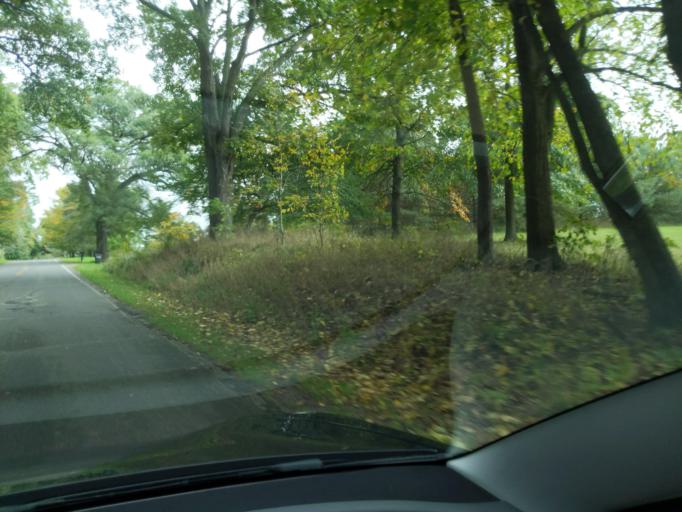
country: US
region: Michigan
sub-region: Ingham County
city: Leslie
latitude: 42.4113
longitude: -84.4043
